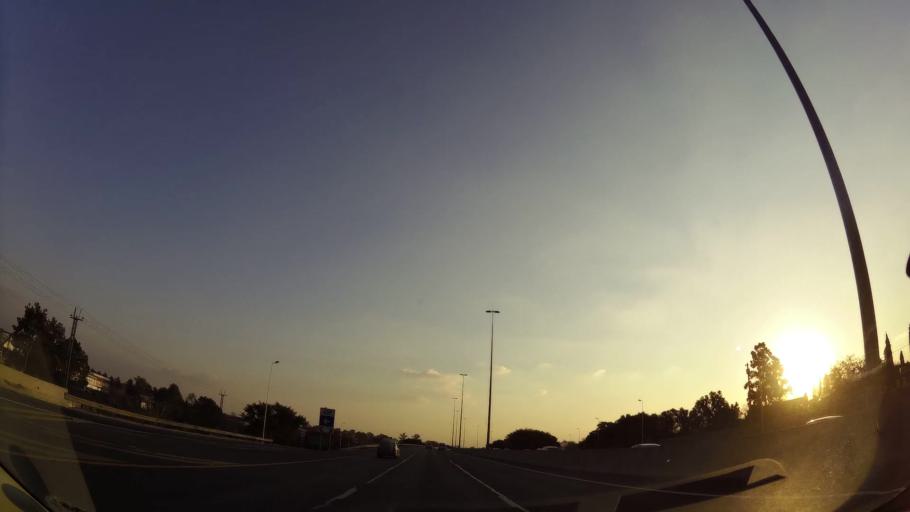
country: ZA
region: Gauteng
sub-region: Ekurhuleni Metropolitan Municipality
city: Benoni
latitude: -26.1812
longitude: 28.3150
